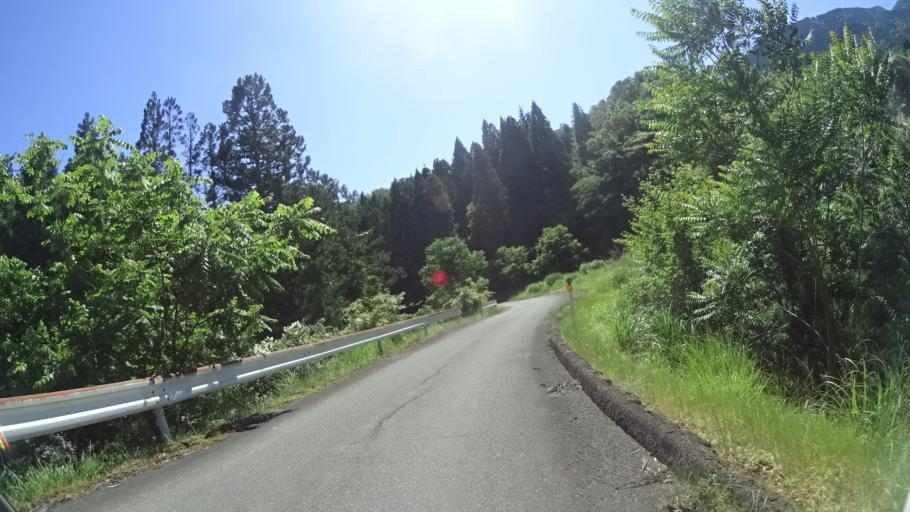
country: JP
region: Kyoto
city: Fukuchiyama
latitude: 35.3845
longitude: 135.0735
